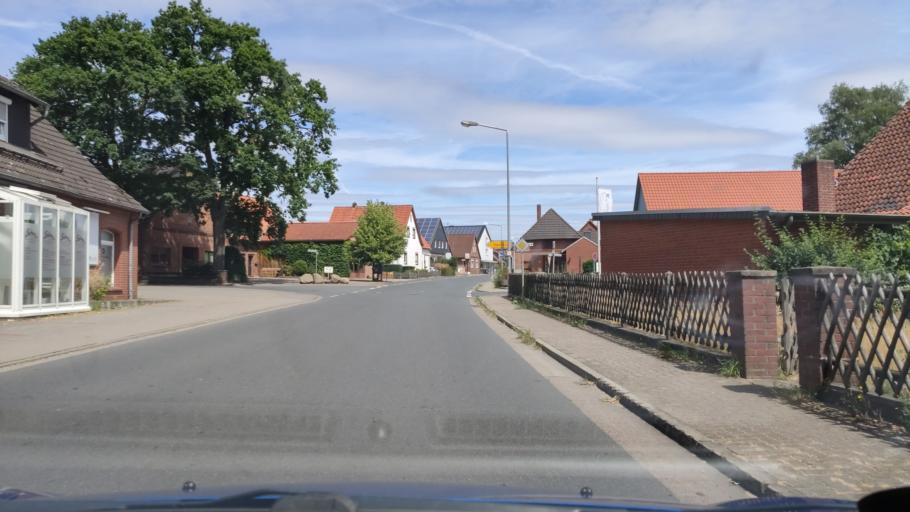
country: DE
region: Lower Saxony
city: Neustadt am Rubenberge
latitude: 52.5601
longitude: 9.4869
